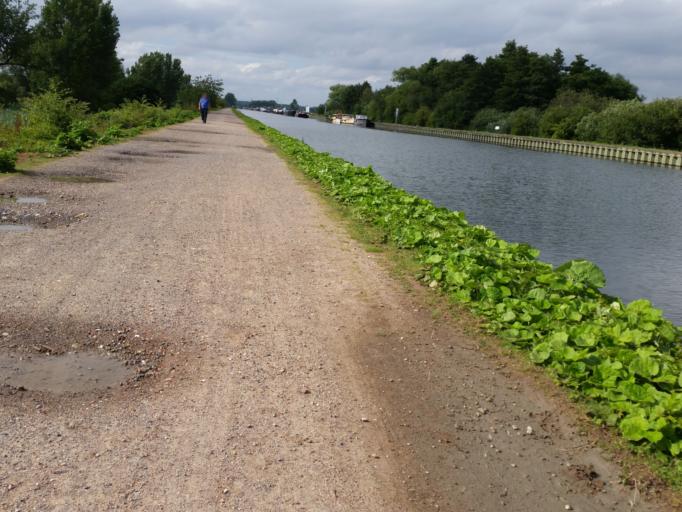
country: BE
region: Flanders
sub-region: Provincie Antwerpen
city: Rumst
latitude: 51.0495
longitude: 4.4351
